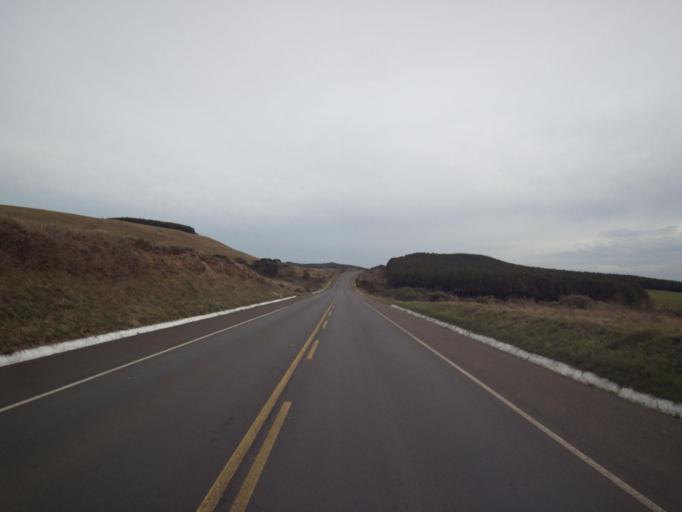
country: BR
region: Parana
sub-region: Palmas
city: Palmas
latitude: -26.6538
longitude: -51.5300
